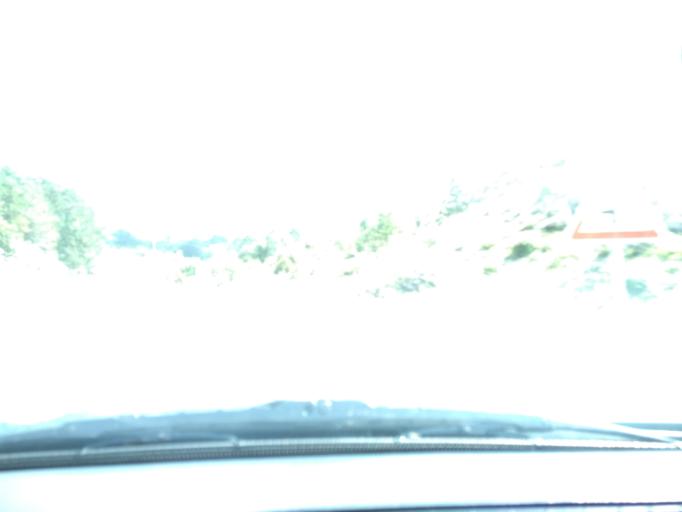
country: ME
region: Kotor
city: Kotor
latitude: 42.4324
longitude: 18.8103
